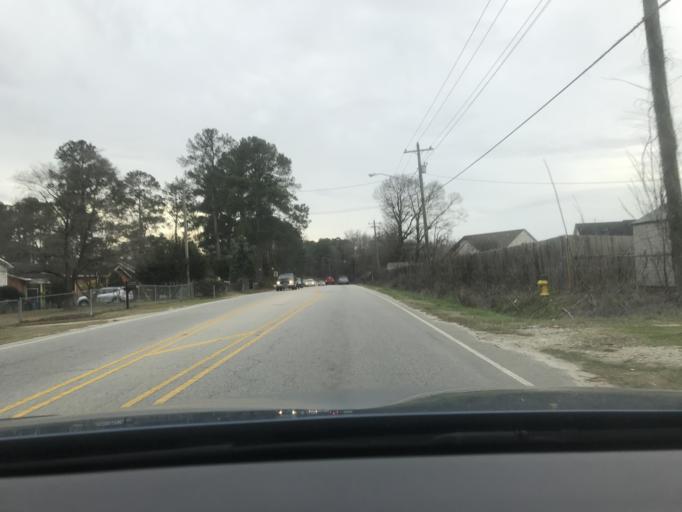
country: US
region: North Carolina
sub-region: Hoke County
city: Rockfish
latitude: 35.0308
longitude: -78.9991
